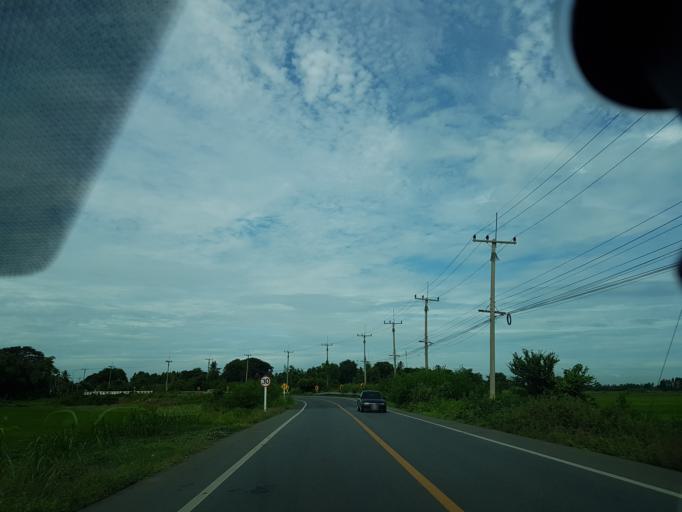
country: TH
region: Lop Buri
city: Tha Wung
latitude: 14.7450
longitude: 100.5438
